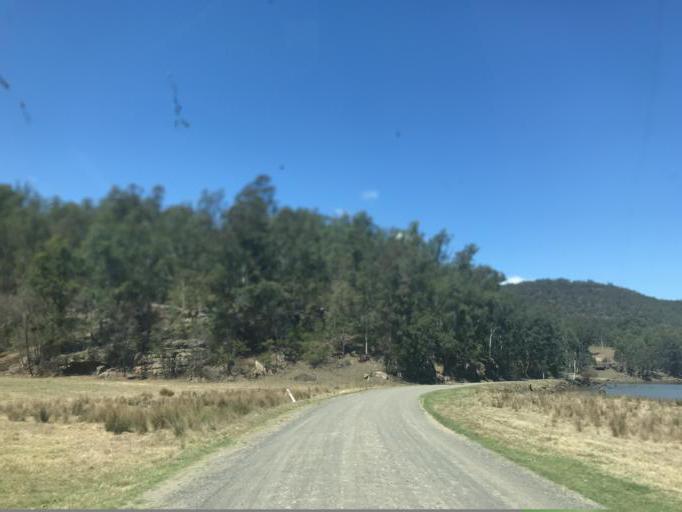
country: AU
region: New South Wales
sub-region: Hornsby Shire
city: Glenorie
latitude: -33.2489
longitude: 150.9765
